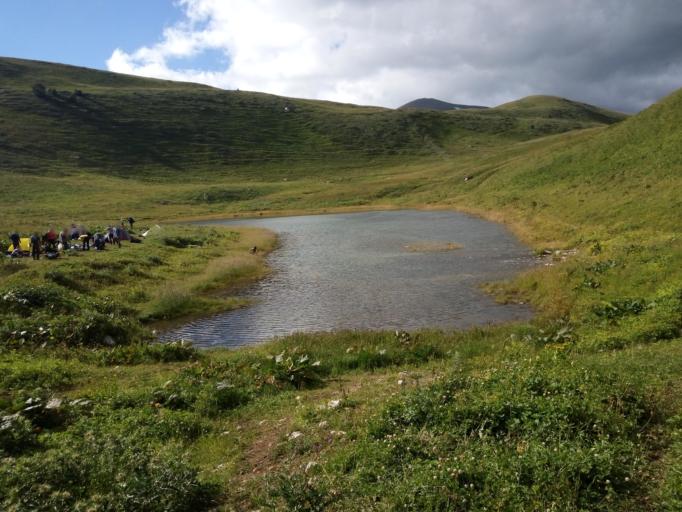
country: RU
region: Adygeya
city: Kamennomostskiy
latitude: 44.0094
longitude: 39.9012
